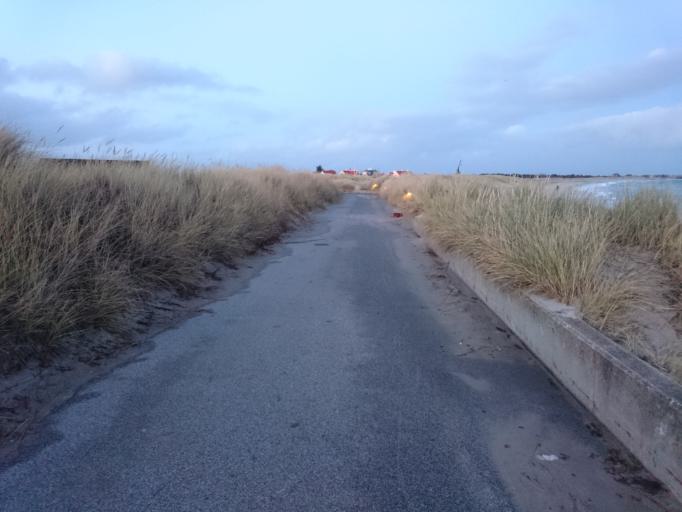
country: DK
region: North Denmark
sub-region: Frederikshavn Kommune
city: Skagen
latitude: 57.7226
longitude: 10.6049
